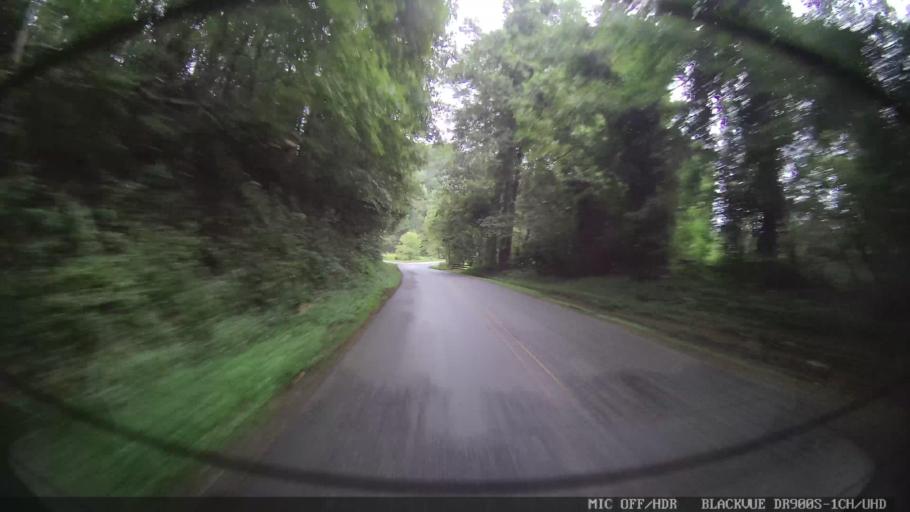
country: US
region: Georgia
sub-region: Gilmer County
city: Ellijay
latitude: 34.7646
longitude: -84.5310
